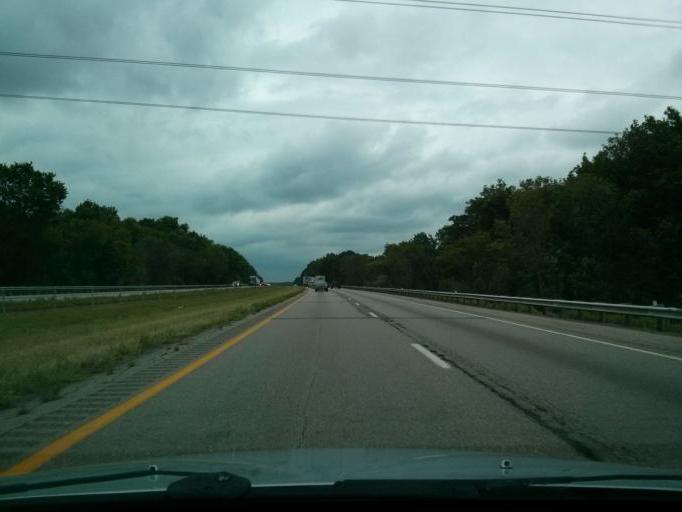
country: US
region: Ohio
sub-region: Portage County
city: Ravenna
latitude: 41.1057
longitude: -81.2074
